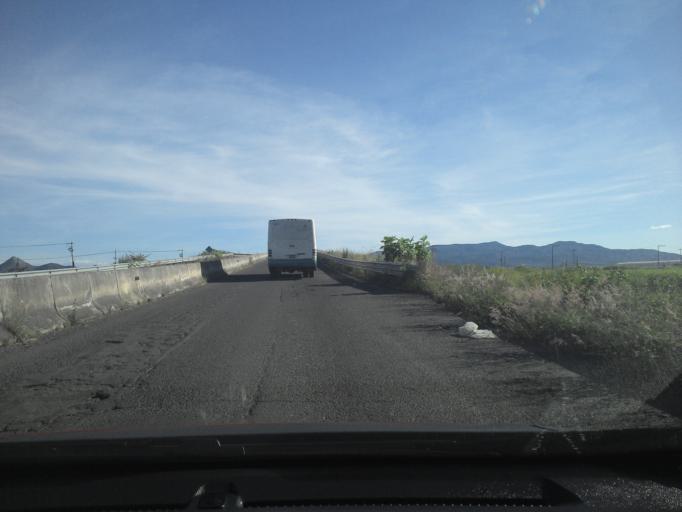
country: MX
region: Jalisco
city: El Refugio
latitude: 20.6592
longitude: -103.7339
